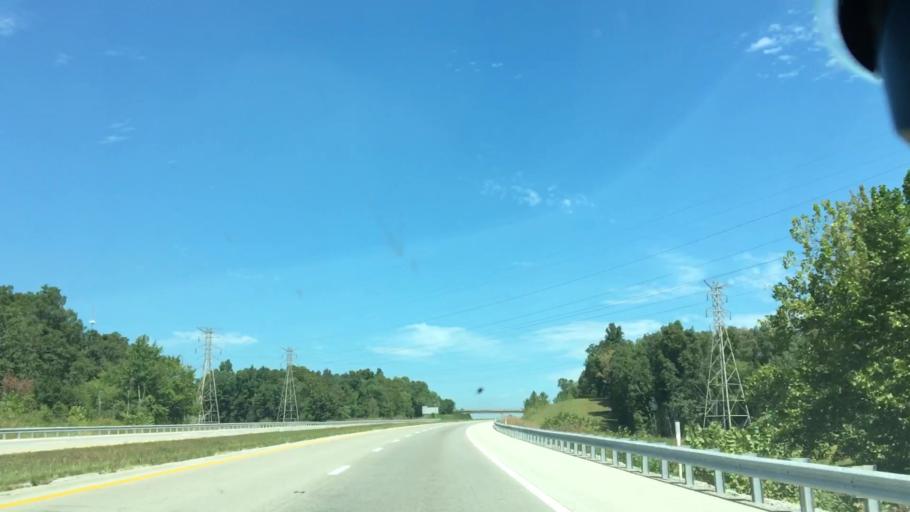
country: US
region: Kentucky
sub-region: Christian County
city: Hopkinsville
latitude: 36.9183
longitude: -87.4739
